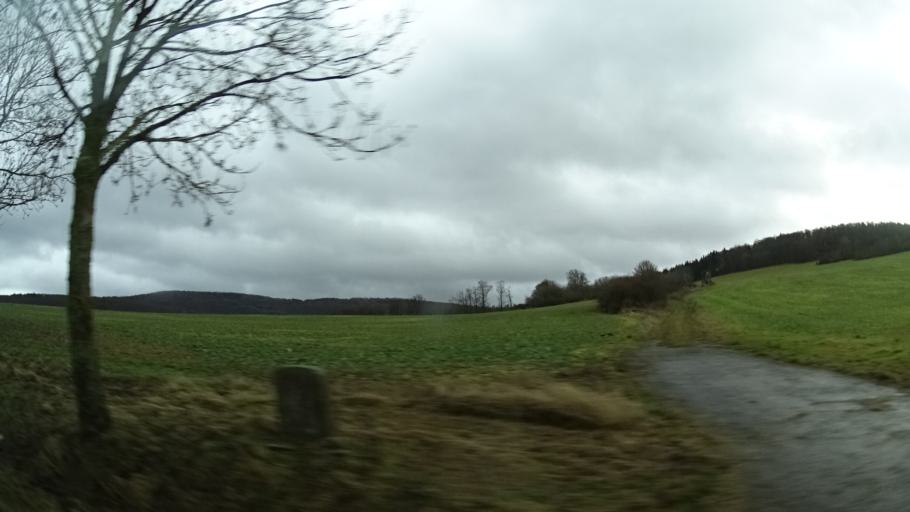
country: DE
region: Thuringia
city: Unterkatz
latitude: 50.6063
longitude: 10.2446
